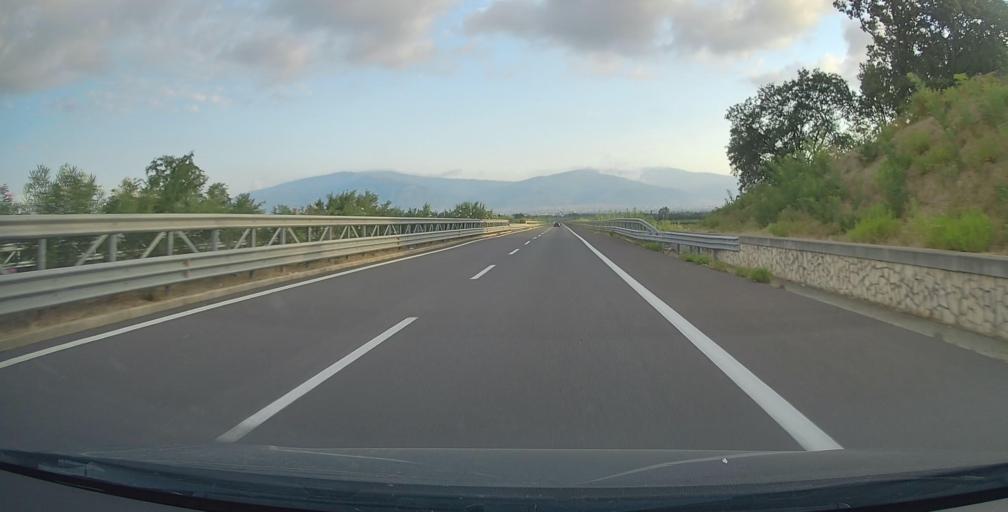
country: IT
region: Calabria
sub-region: Provincia di Catanzaro
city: Acconia
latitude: 38.8750
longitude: 16.2819
